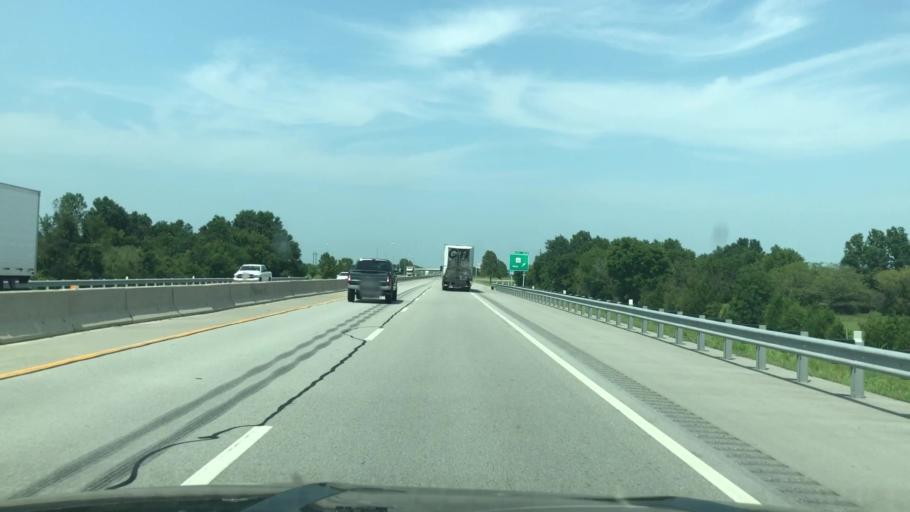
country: US
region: Oklahoma
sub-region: Ottawa County
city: Miami
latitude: 36.8582
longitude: -94.8532
